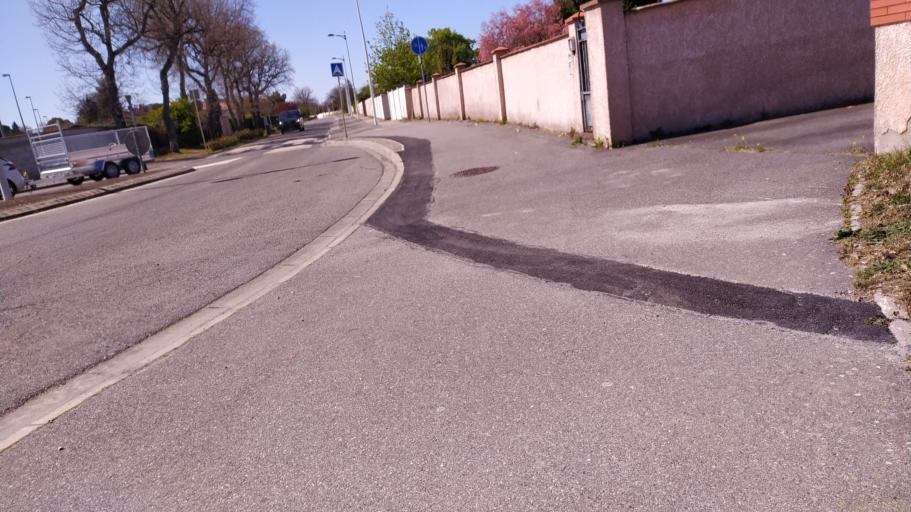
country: FR
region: Midi-Pyrenees
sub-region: Departement de la Haute-Garonne
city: Tournefeuille
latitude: 43.5865
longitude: 1.3173
